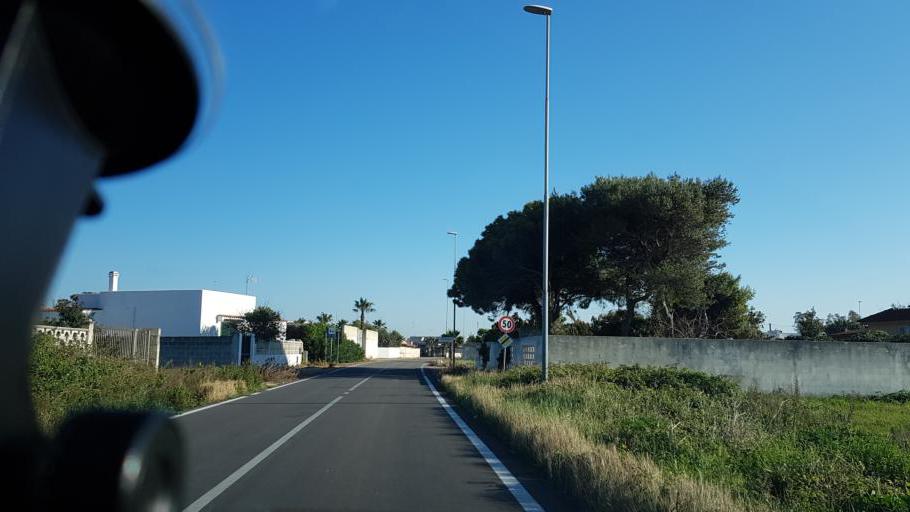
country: IT
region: Apulia
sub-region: Provincia di Lecce
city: Merine
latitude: 40.4320
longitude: 18.2416
